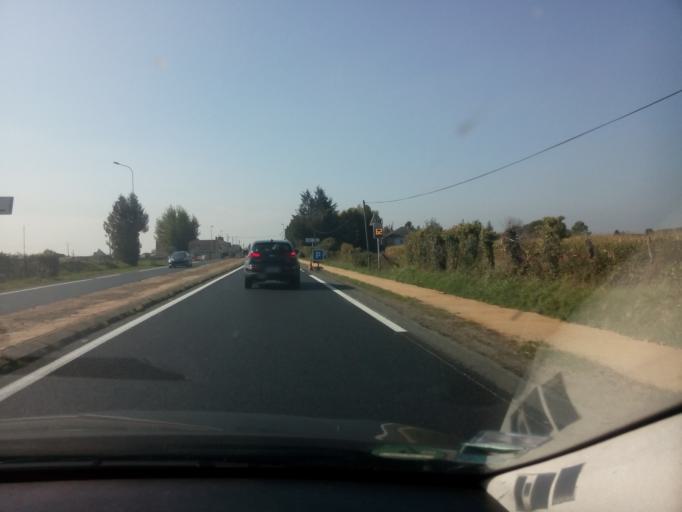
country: FR
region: Pays de la Loire
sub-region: Departement de Maine-et-Loire
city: Corze
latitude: 47.5558
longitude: -0.3800
